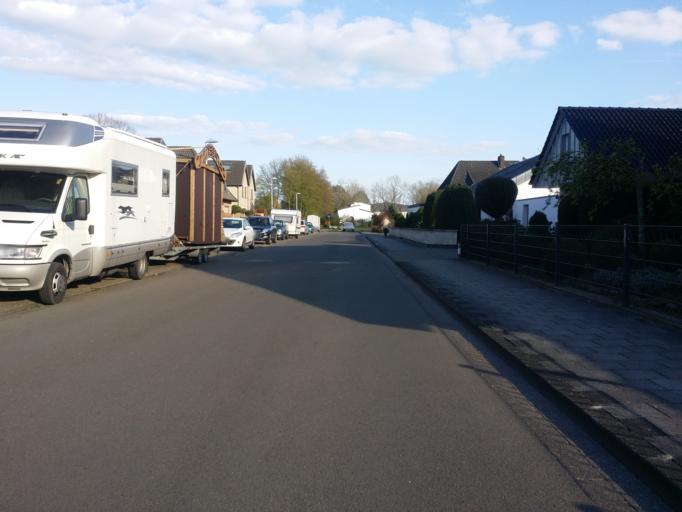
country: DE
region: Lower Saxony
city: Delmenhorst
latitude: 53.0287
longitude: 8.6231
